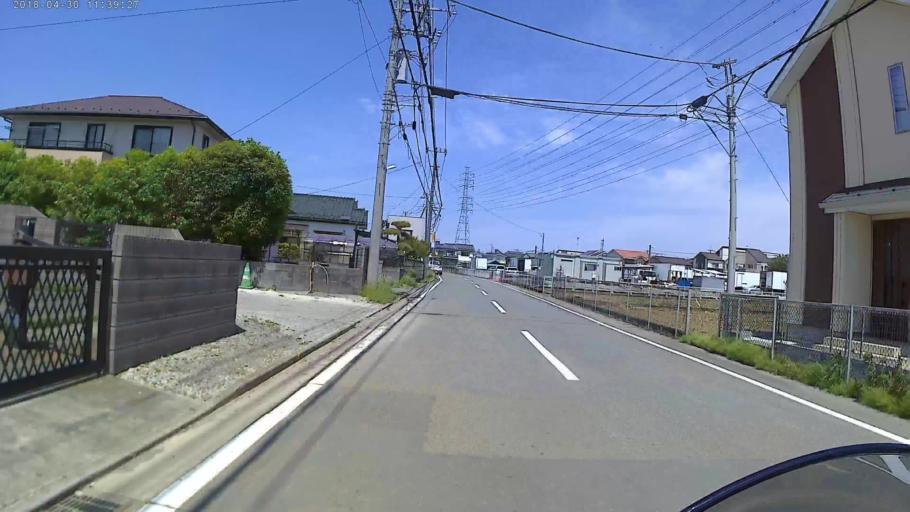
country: JP
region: Kanagawa
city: Zama
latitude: 35.4813
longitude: 139.3894
